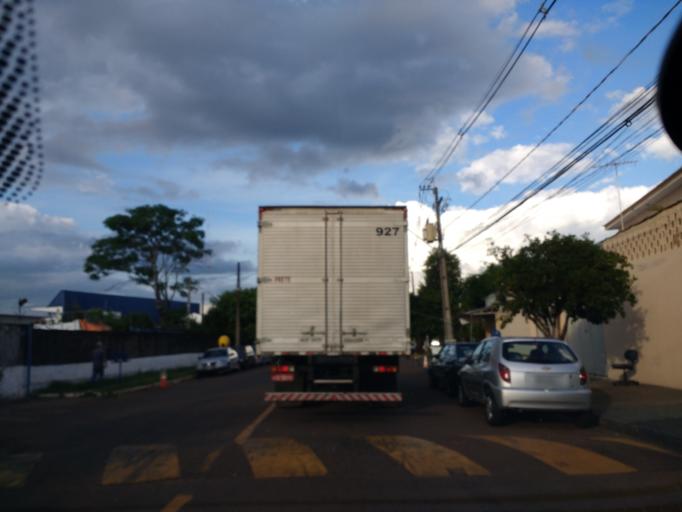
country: BR
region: Parana
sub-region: Londrina
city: Londrina
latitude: -23.2951
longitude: -51.1704
